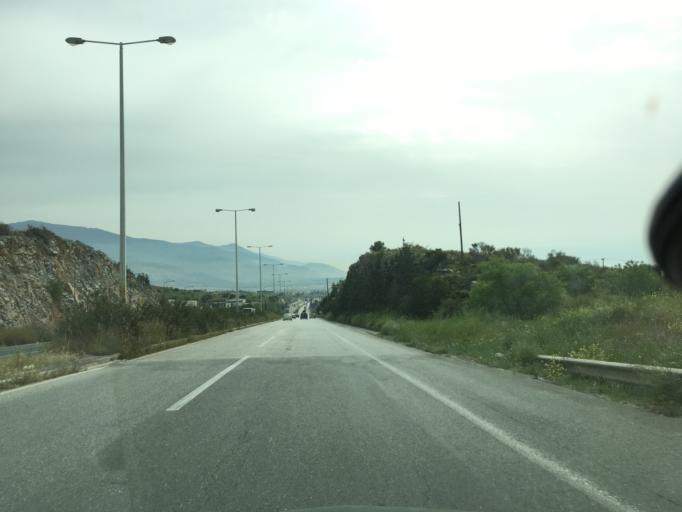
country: GR
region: Thessaly
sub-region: Nomos Magnisias
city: Nea Ionia
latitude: 39.3770
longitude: 22.8867
